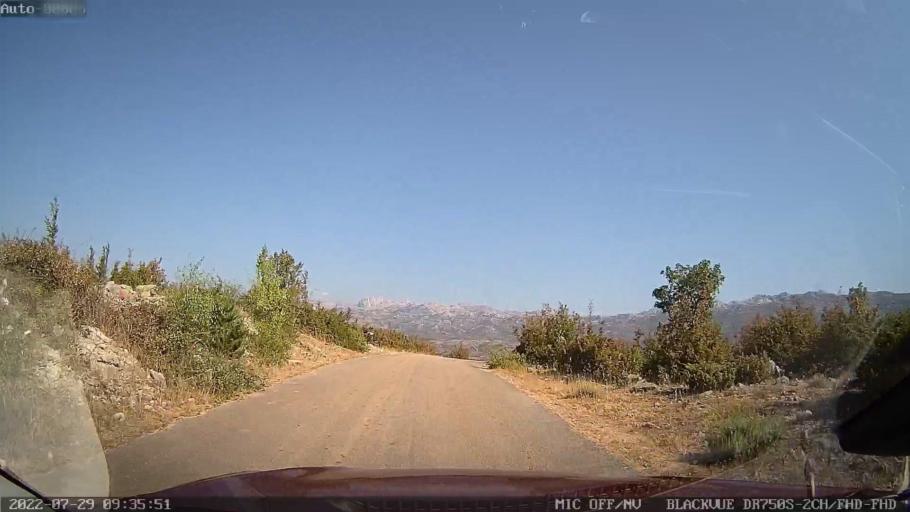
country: HR
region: Zadarska
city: Obrovac
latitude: 44.1883
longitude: 15.7331
